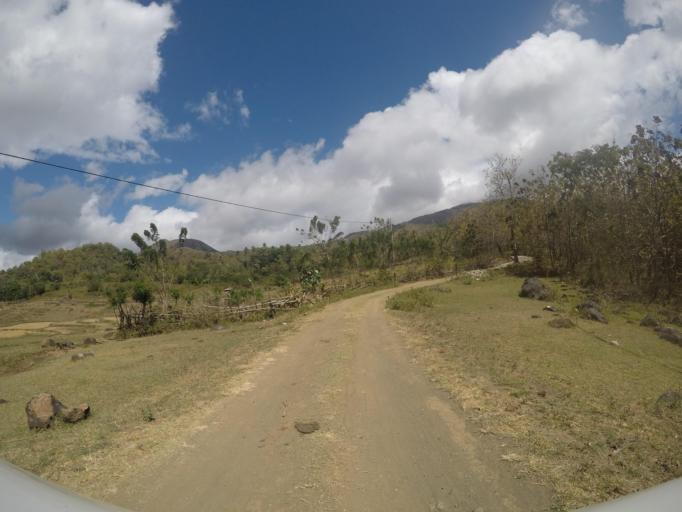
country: TL
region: Lautem
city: Lospalos
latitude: -8.5311
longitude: 126.7995
